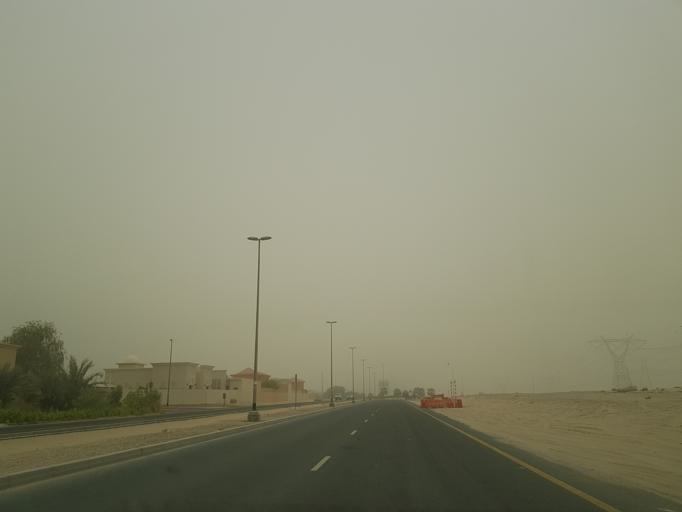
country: AE
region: Dubai
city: Dubai
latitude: 25.1560
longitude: 55.2755
